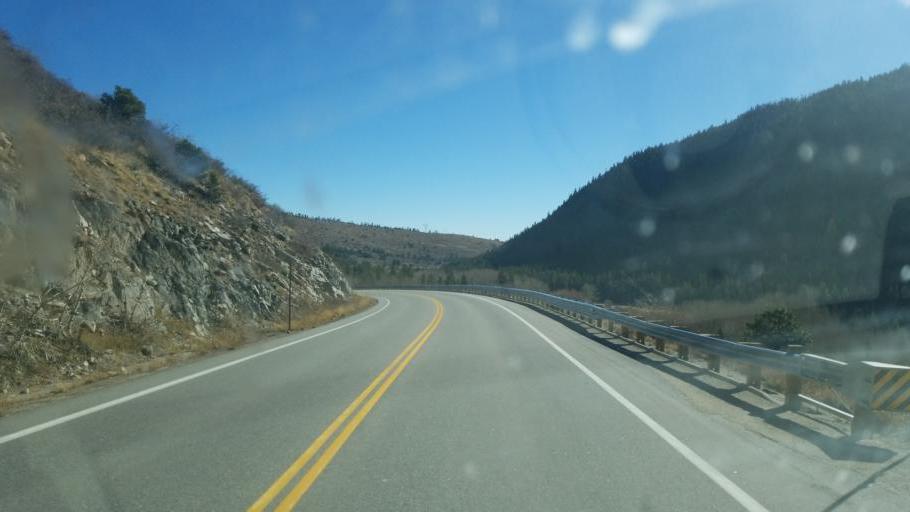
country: US
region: Colorado
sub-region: Chaffee County
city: Salida
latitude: 38.5496
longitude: -106.2699
